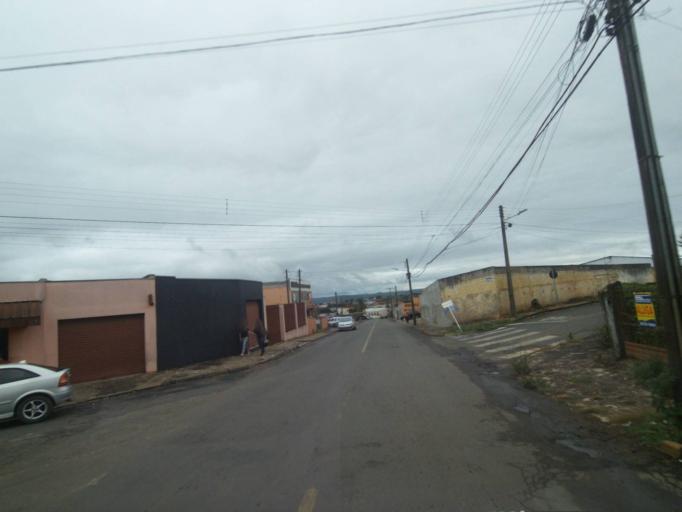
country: BR
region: Parana
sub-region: Telemaco Borba
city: Telemaco Borba
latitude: -24.3282
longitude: -50.6433
